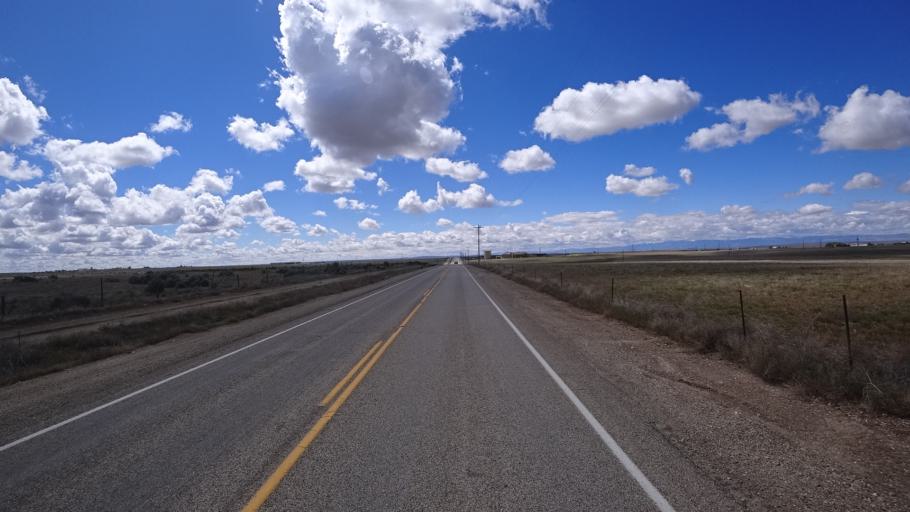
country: US
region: Idaho
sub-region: Ada County
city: Boise
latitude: 43.4674
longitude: -116.2343
